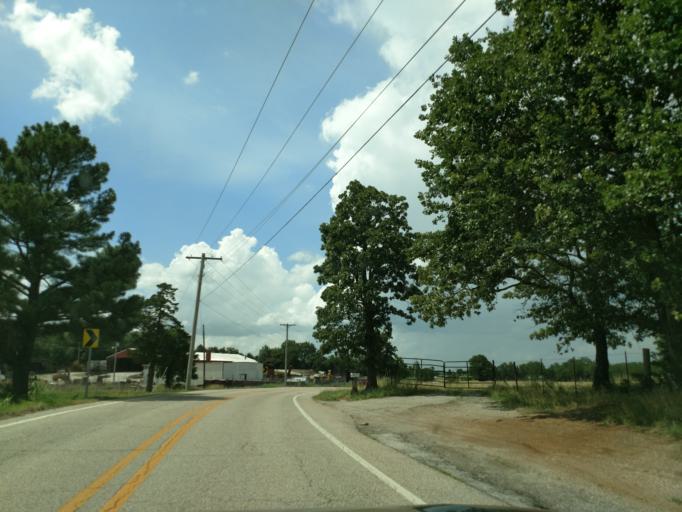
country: US
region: Arkansas
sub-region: Boone County
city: Harrison
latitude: 36.2665
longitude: -93.2314
